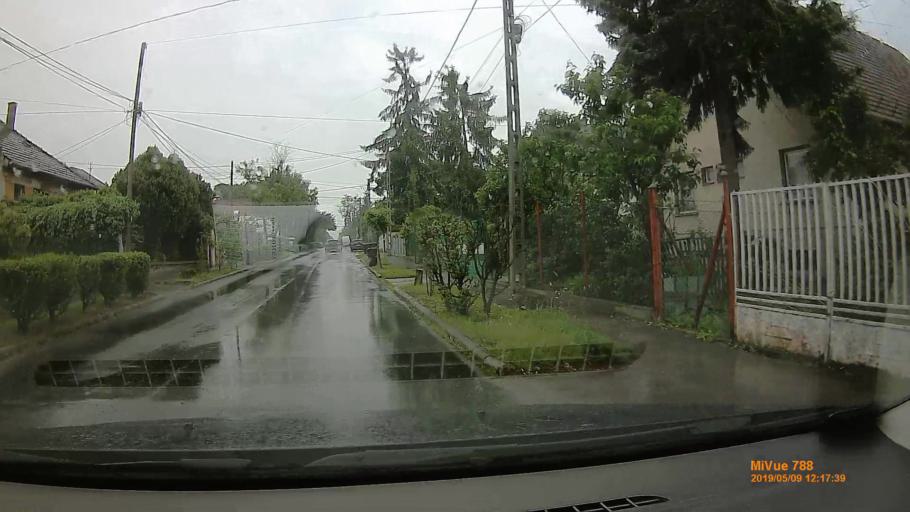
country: HU
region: Budapest
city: Budapest XVI. keruelet
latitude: 47.5232
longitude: 19.1582
